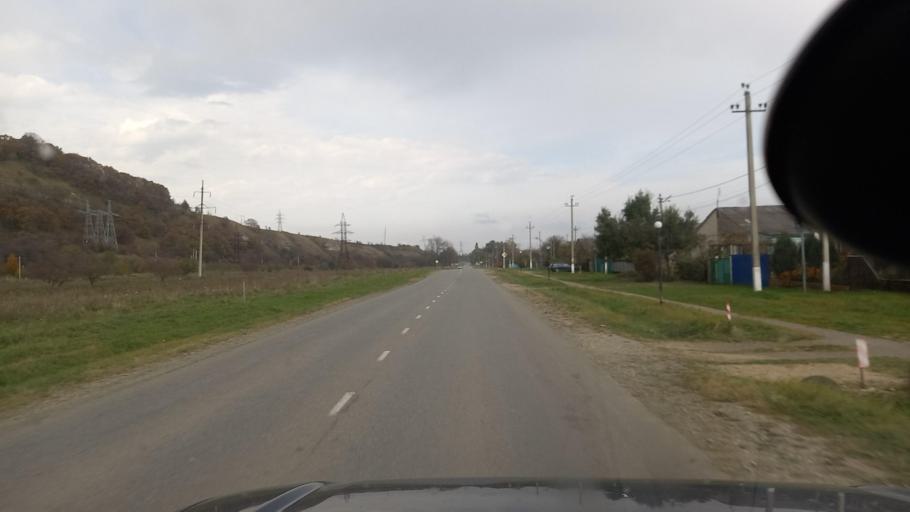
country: RU
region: Krasnodarskiy
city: Psebay
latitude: 44.1561
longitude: 40.8340
